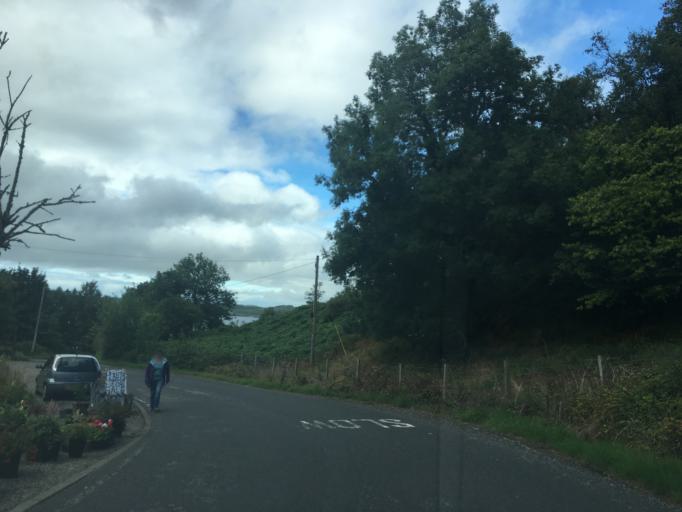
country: GB
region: Scotland
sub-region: Argyll and Bute
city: Ardrishaig
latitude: 56.0898
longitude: -5.5600
